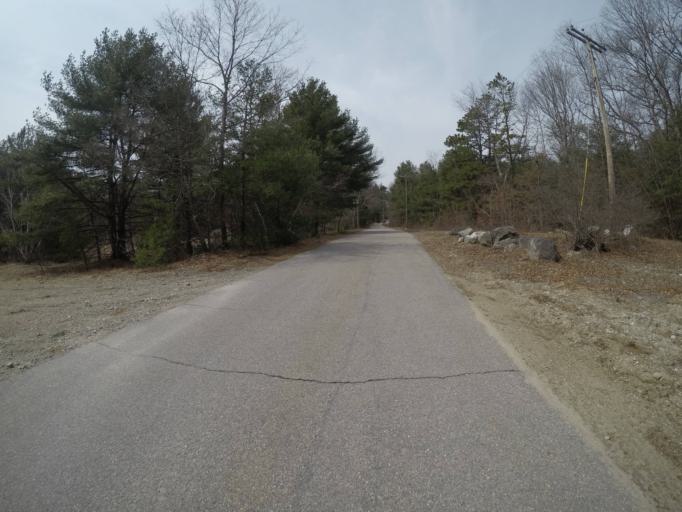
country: US
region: Massachusetts
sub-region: Bristol County
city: Easton
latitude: 42.0503
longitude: -71.0962
